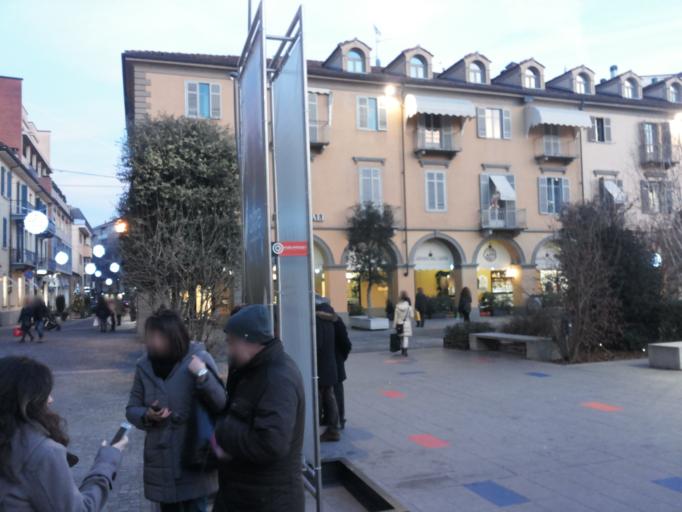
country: IT
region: Piedmont
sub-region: Provincia di Cuneo
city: Alba
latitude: 44.6972
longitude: 8.0344
